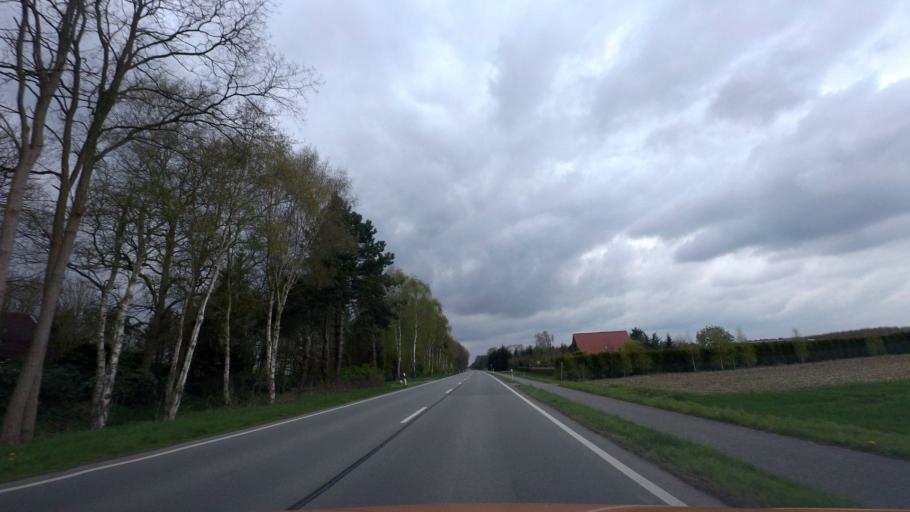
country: DE
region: Lower Saxony
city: Bosel
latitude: 53.0693
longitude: 7.9236
